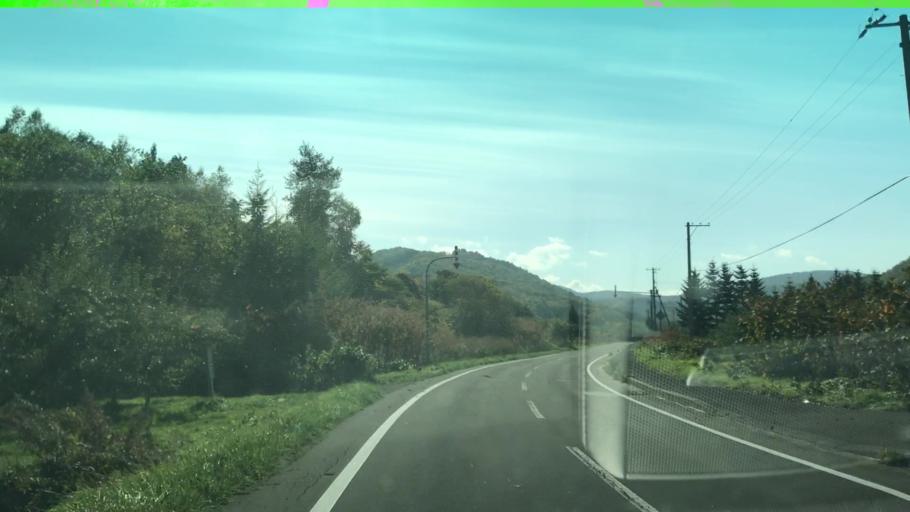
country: JP
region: Hokkaido
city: Yoichi
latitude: 43.1603
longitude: 140.8218
